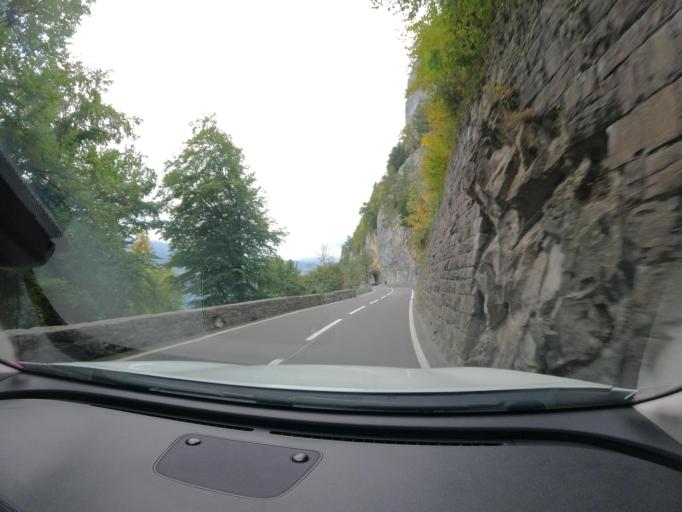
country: CH
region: Bern
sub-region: Interlaken-Oberhasli District
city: Beatenberg
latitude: 46.6826
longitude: 7.7620
